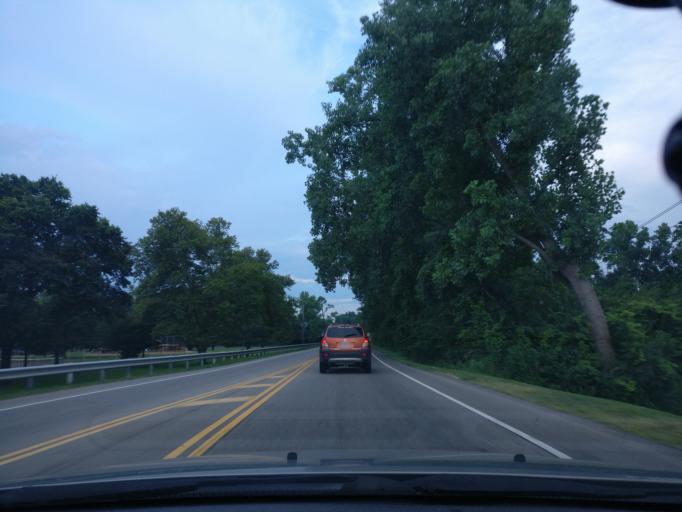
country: US
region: Ohio
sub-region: Warren County
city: Franklin
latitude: 39.5536
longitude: -84.2993
